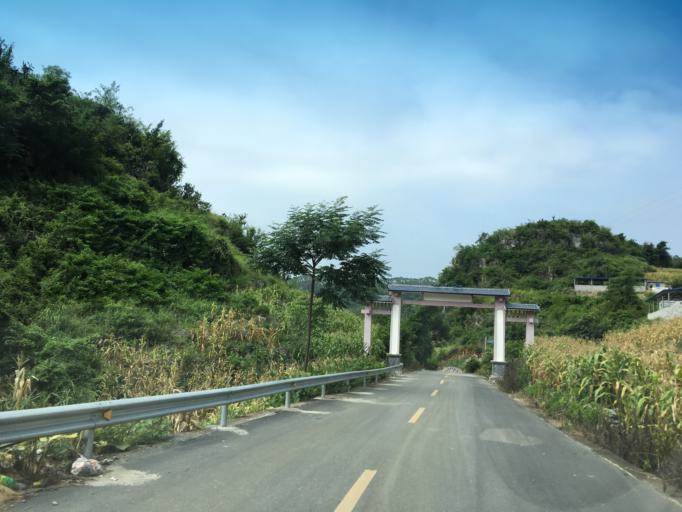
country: CN
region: Guangxi Zhuangzu Zizhiqu
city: Xinzhou
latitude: 24.8250
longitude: 105.6472
